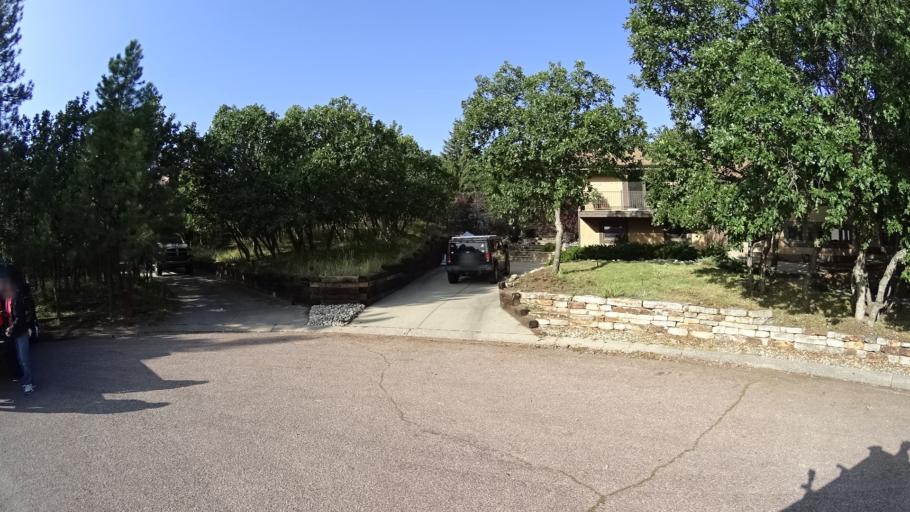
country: US
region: Colorado
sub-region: El Paso County
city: Colorado Springs
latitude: 38.8221
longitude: -104.8721
